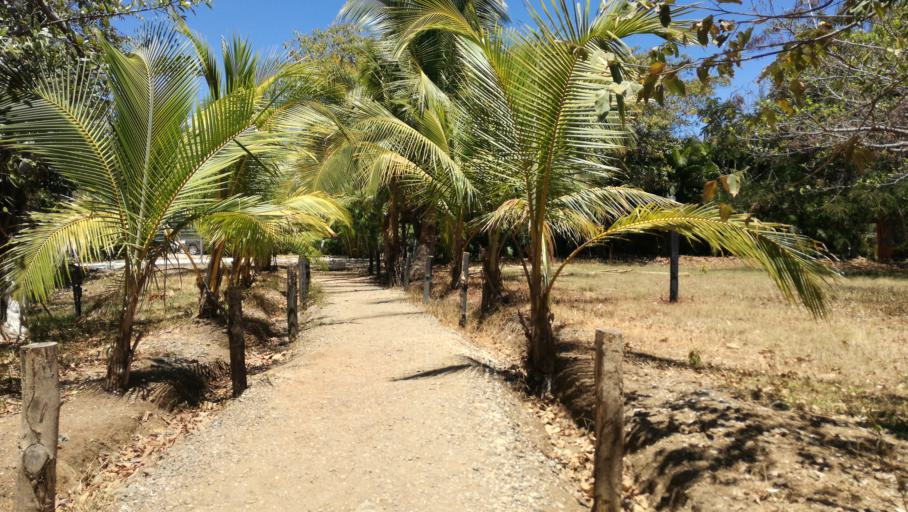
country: CR
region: Guanacaste
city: Samara
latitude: 9.8630
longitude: -85.4444
